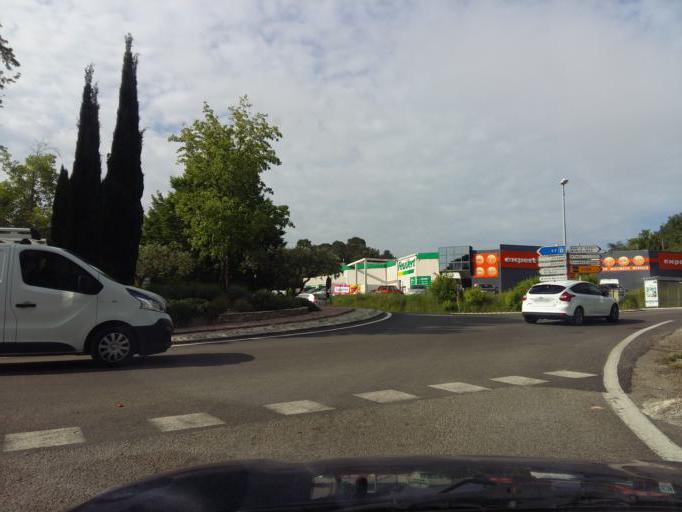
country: FR
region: Languedoc-Roussillon
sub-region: Departement du Gard
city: Bagnols-sur-Ceze
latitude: 44.1586
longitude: 4.6323
